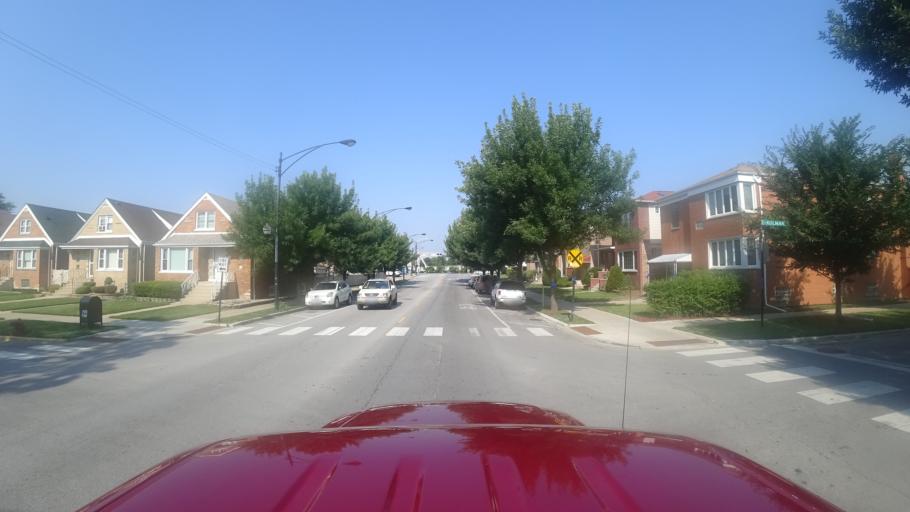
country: US
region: Illinois
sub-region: Cook County
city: Hometown
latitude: 41.7858
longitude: -87.7363
